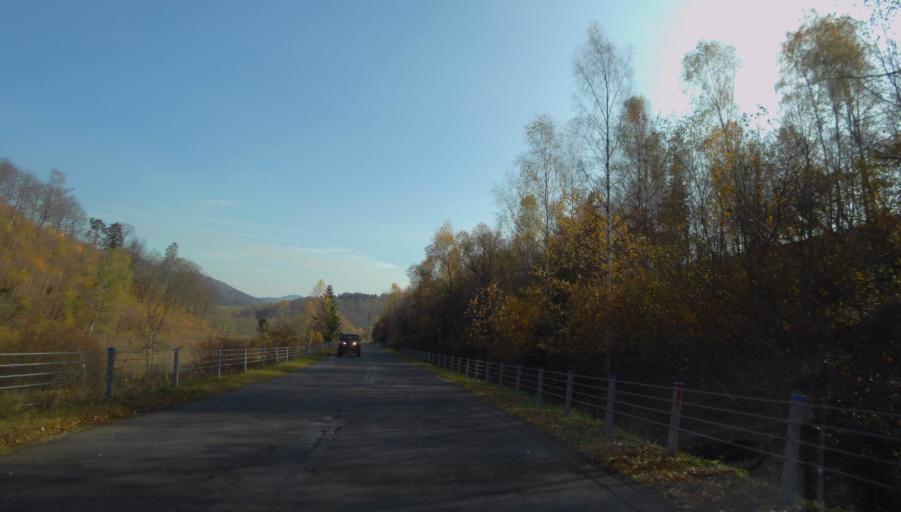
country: PL
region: Subcarpathian Voivodeship
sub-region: Powiat leski
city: Cisna
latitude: 49.2072
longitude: 22.2523
